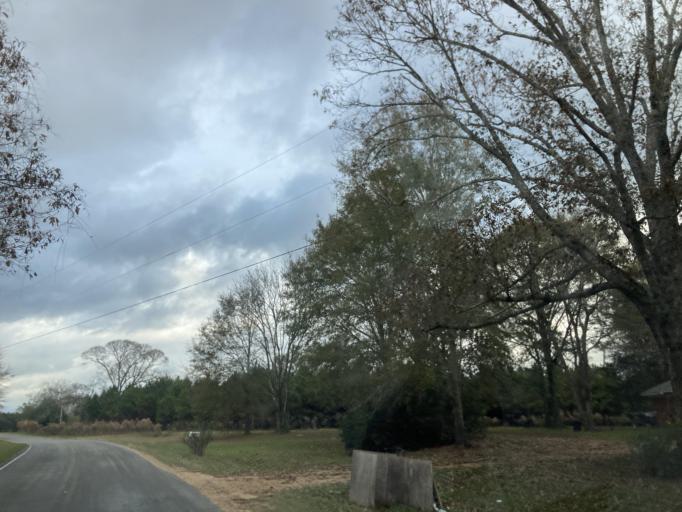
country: US
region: Mississippi
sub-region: Marion County
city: Columbia
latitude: 31.1889
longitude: -89.6661
